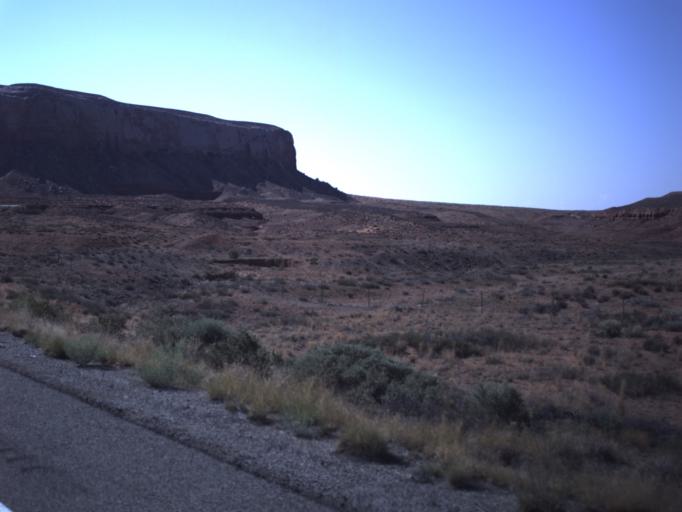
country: US
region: Utah
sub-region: San Juan County
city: Blanding
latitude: 37.2465
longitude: -109.6089
